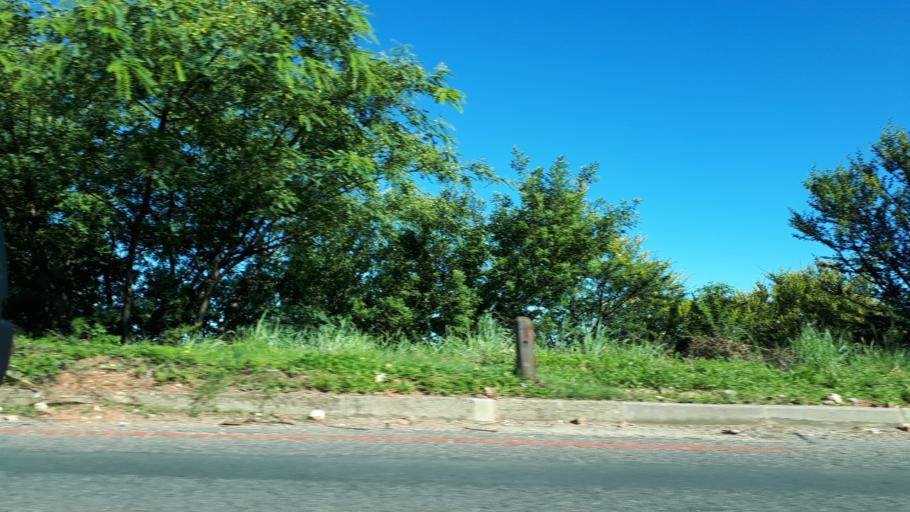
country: ZA
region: Gauteng
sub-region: Ekurhuleni Metropolitan Municipality
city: Germiston
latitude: -26.1734
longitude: 28.1604
